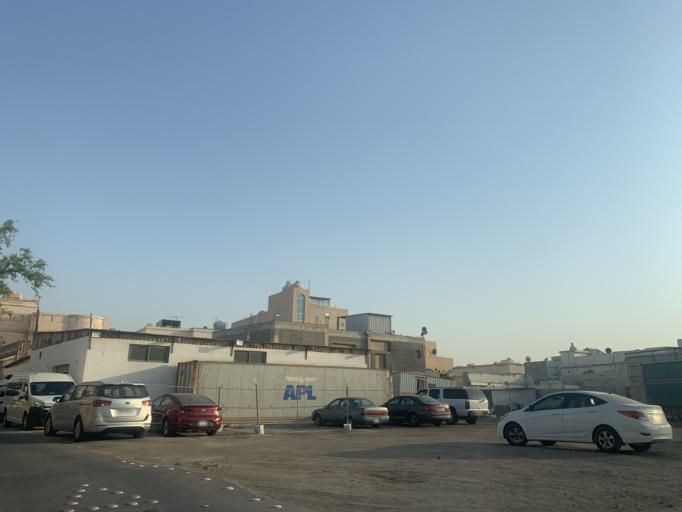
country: BH
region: Manama
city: Jidd Hafs
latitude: 26.2156
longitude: 50.5315
